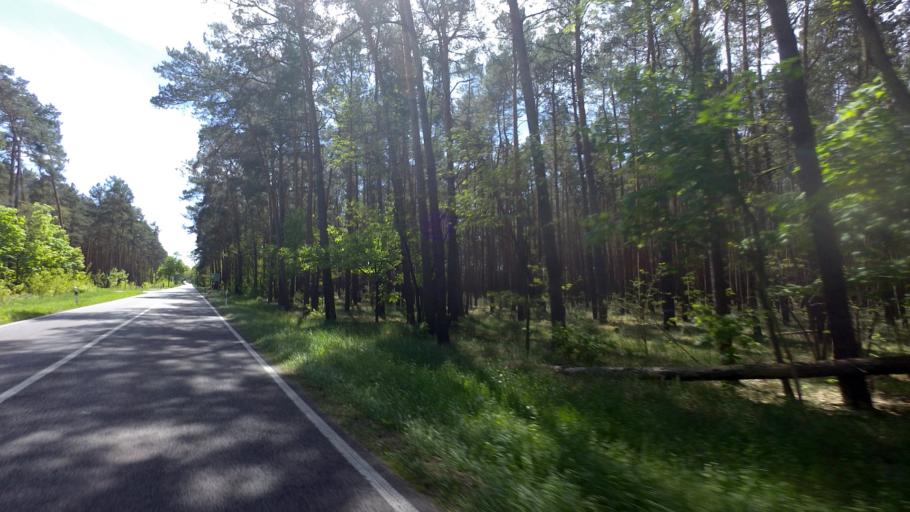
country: DE
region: Brandenburg
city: Luckenwalde
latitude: 52.1545
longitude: 13.1056
